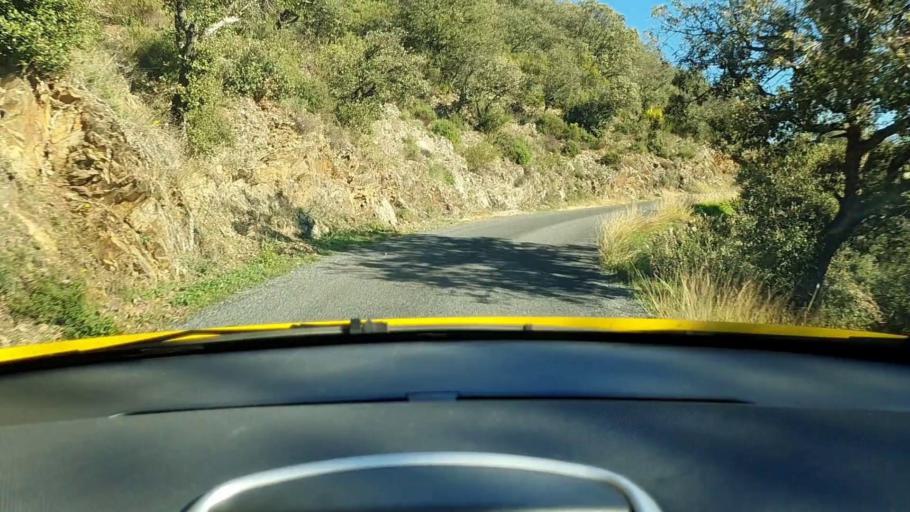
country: FR
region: Languedoc-Roussillon
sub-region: Departement du Gard
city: Sumene
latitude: 44.0324
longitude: 3.7004
